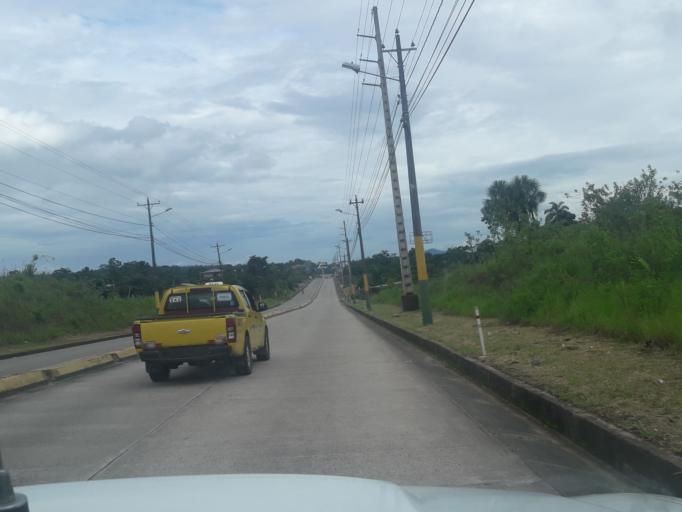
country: EC
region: Napo
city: Archidona
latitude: -0.9503
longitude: -77.8169
